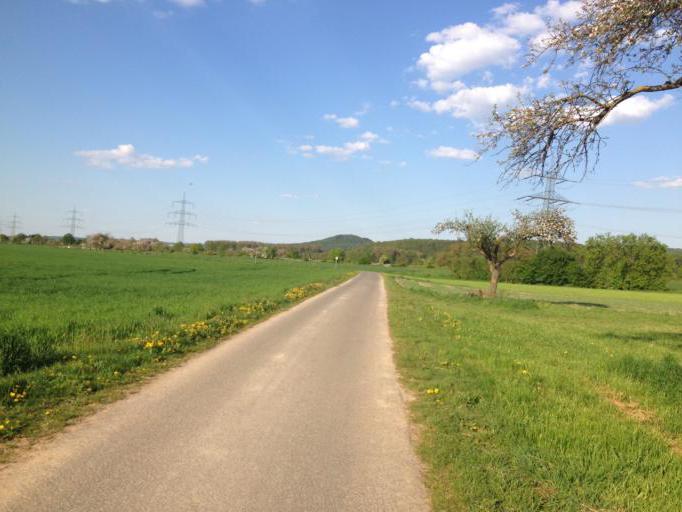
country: DE
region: Hesse
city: Lollar
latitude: 50.6259
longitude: 8.6768
